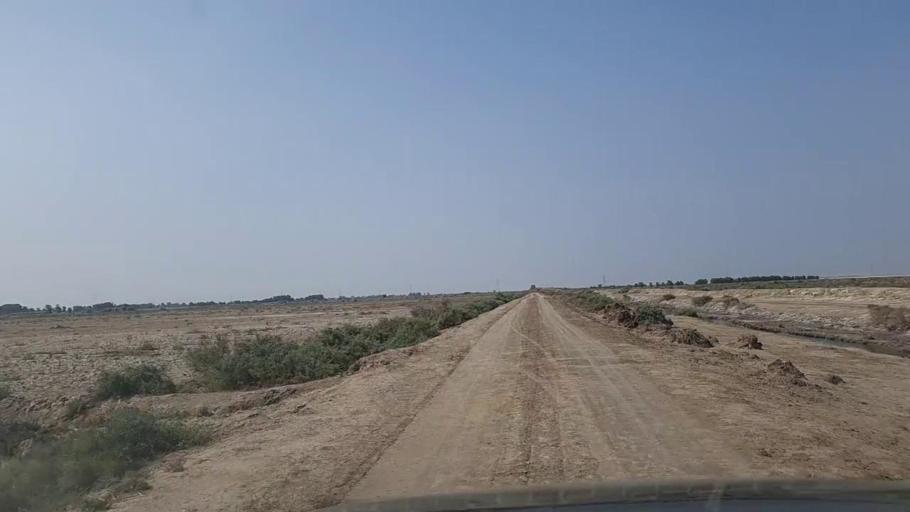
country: PK
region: Sindh
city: Gharo
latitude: 24.7046
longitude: 67.5639
